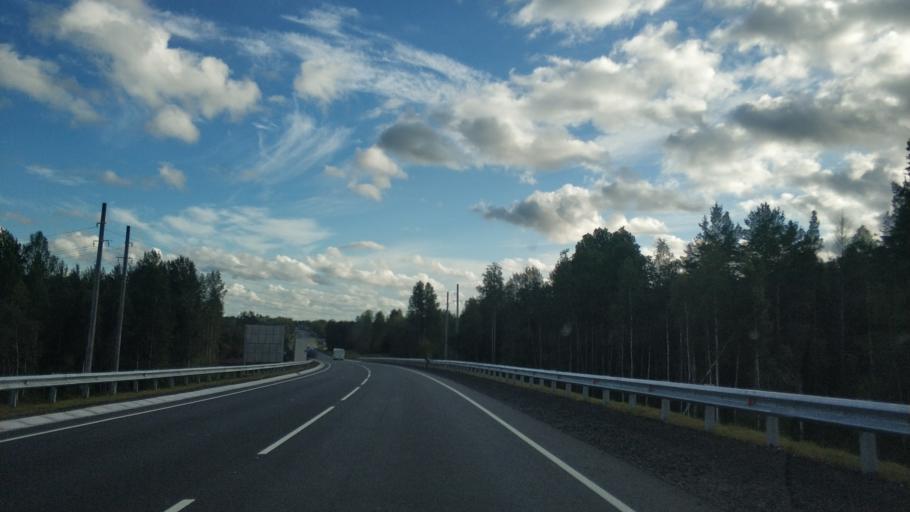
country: RU
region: Leningrad
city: Priozersk
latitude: 60.8391
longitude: 30.1236
